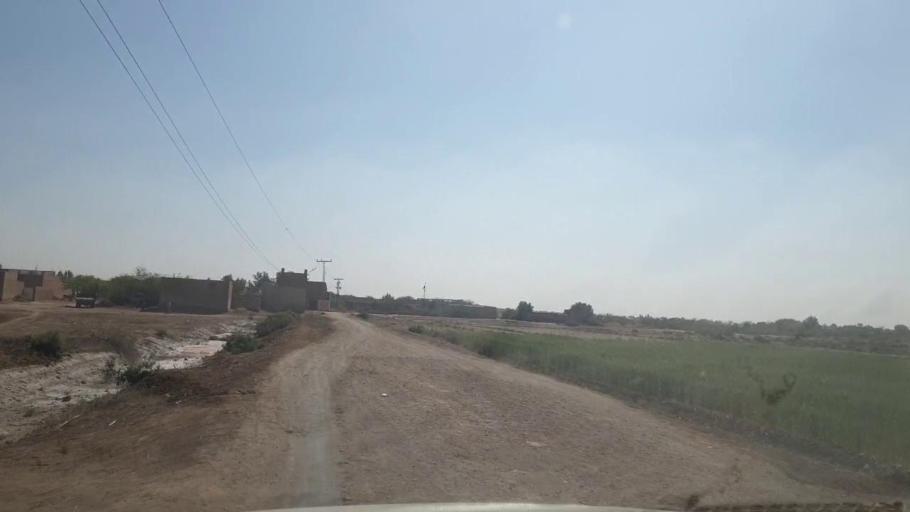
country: PK
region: Sindh
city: Mirpur Khas
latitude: 25.5056
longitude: 69.0847
